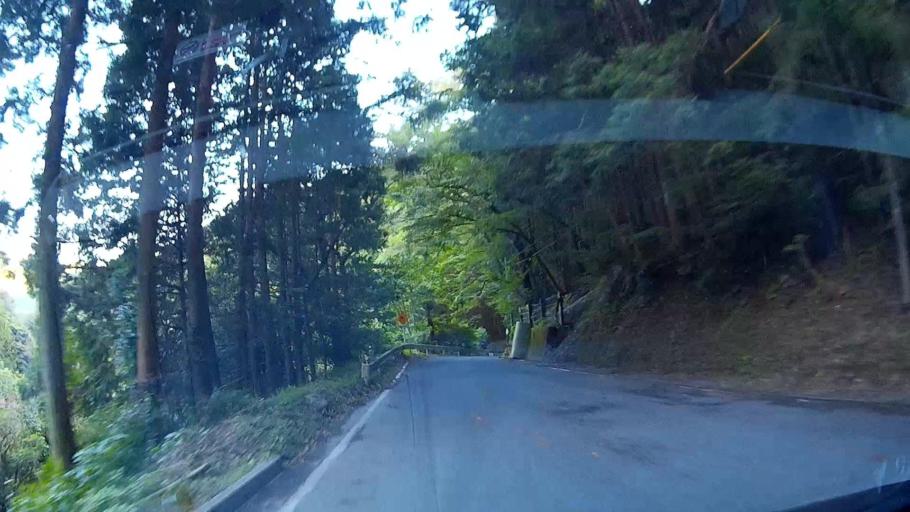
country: JP
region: Shizuoka
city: Shizuoka-shi
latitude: 35.1344
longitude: 138.2805
